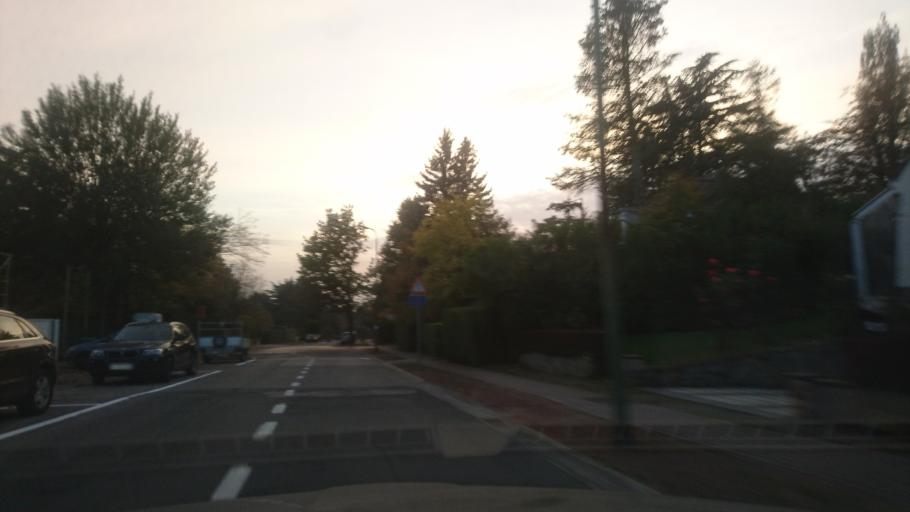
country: BE
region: Flanders
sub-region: Provincie Vlaams-Brabant
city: Sint-Genesius-Rode
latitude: 50.7560
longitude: 4.3662
